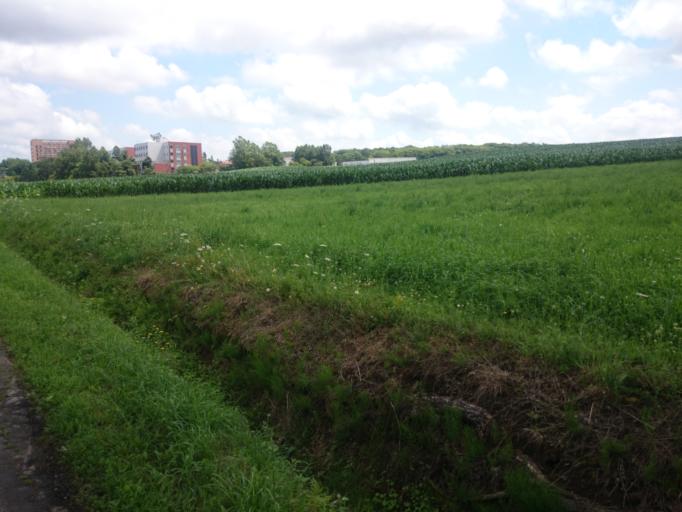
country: JP
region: Hokkaido
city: Ebetsu
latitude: 43.0703
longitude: 141.5033
